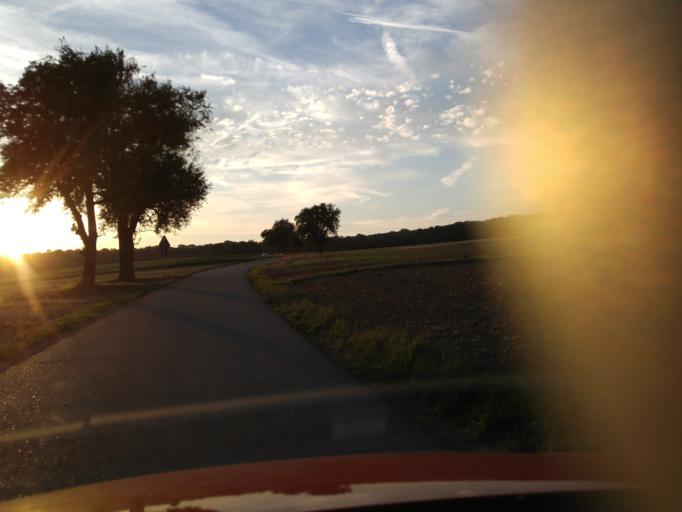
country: DE
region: Baden-Wuerttemberg
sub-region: Regierungsbezirk Stuttgart
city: Untereisesheim
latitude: 49.2033
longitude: 9.1793
